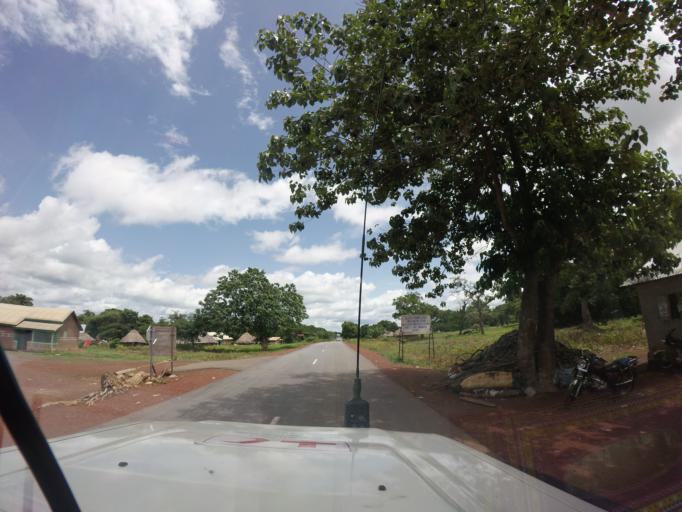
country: SL
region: Northern Province
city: Gberia Fotombu
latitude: 10.0541
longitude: -11.0678
